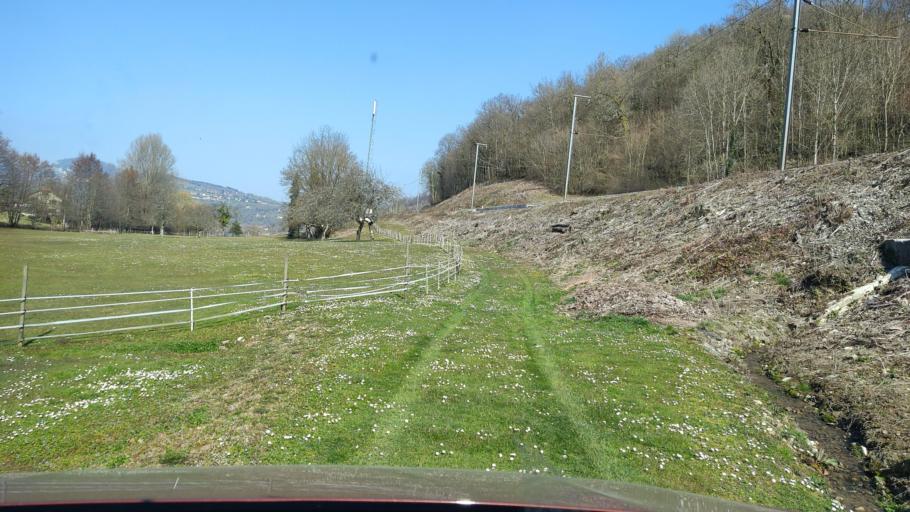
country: FR
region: Rhone-Alpes
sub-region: Departement de la Savoie
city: Saint-Beron
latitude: 45.5103
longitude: 5.7386
